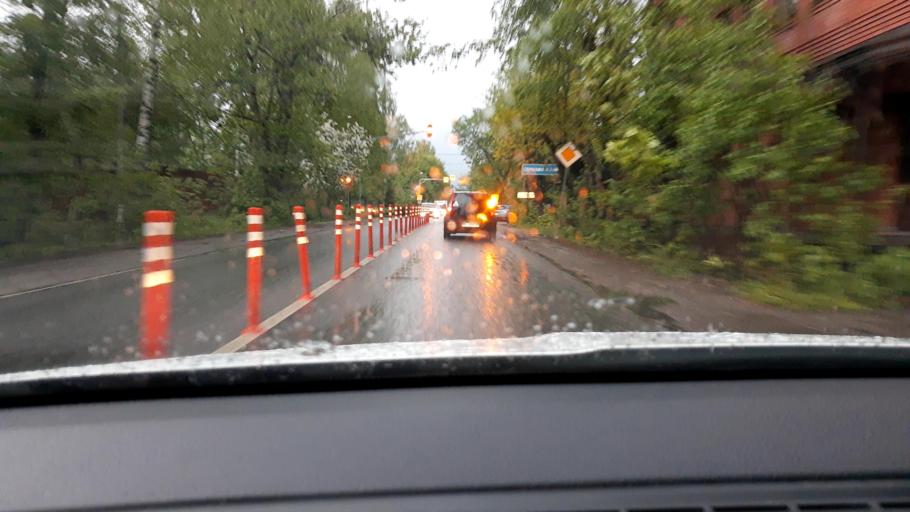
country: RU
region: Moskovskaya
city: Zagoryanskiy
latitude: 55.9135
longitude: 37.9164
